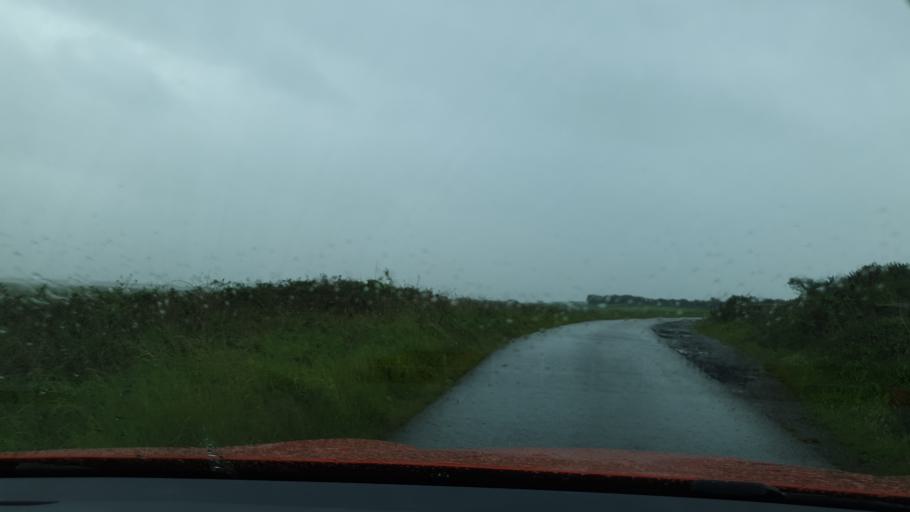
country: GB
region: England
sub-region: Cumbria
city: Barrow in Furness
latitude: 54.0630
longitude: -3.2112
